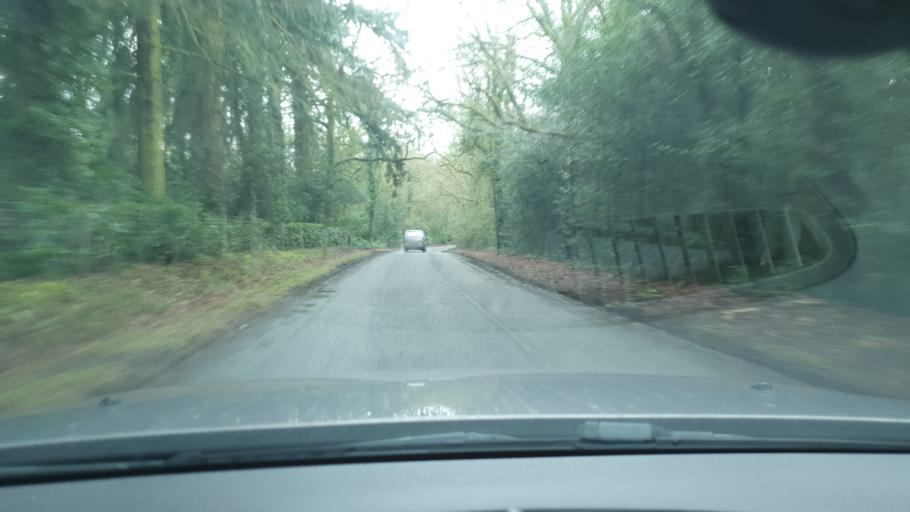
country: GB
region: England
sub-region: West Berkshire
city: Greenham
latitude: 51.3555
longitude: -1.3133
